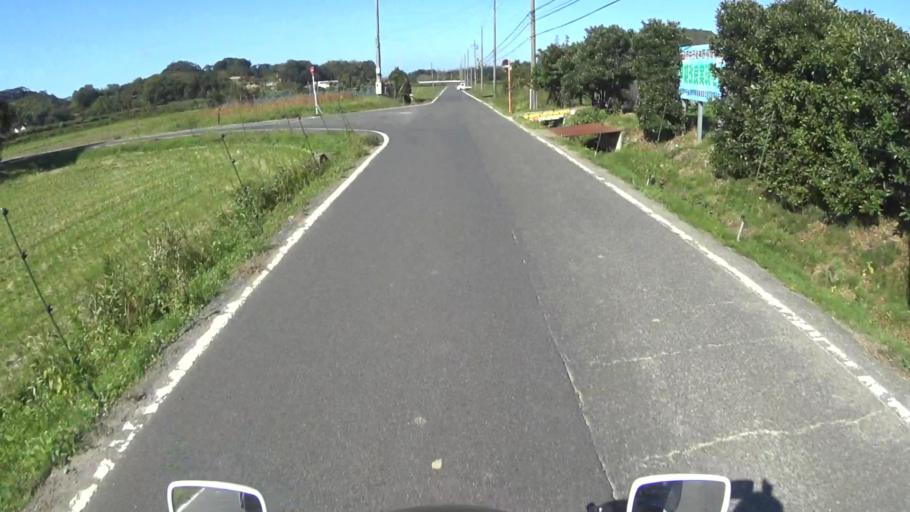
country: JP
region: Hyogo
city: Toyooka
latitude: 35.6346
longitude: 134.9456
